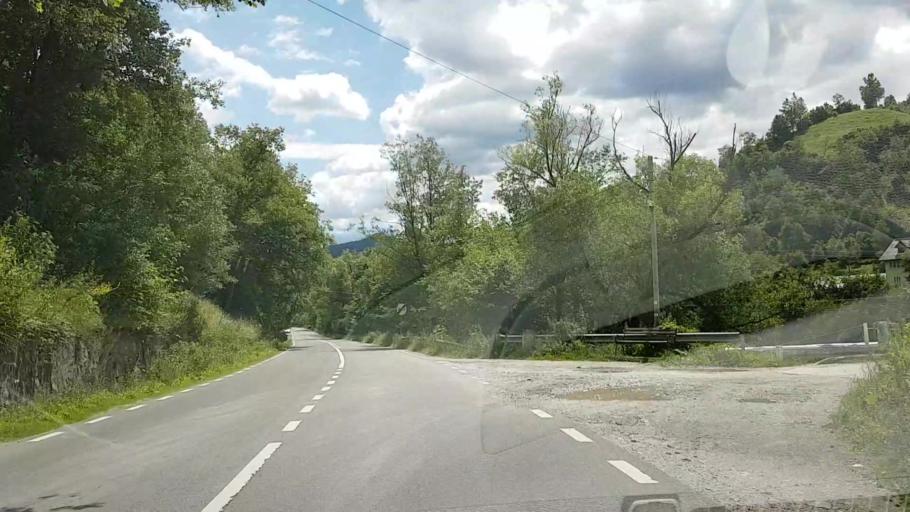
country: RO
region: Suceava
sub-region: Comuna Brosteni
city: Brosteni
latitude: 47.2589
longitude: 25.6903
